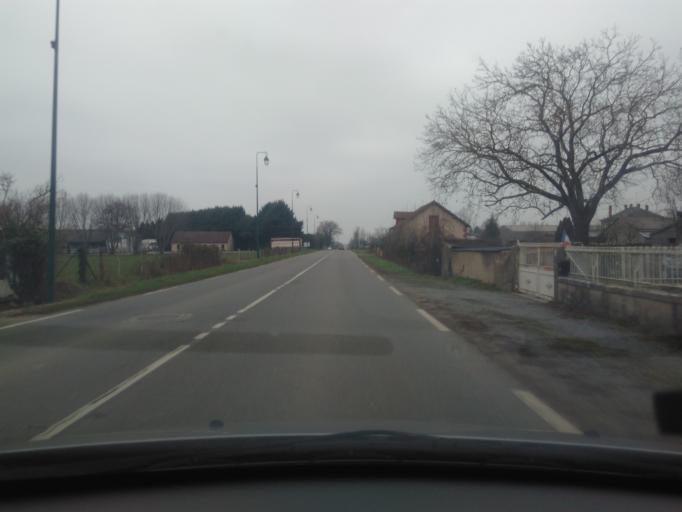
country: FR
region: Centre
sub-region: Departement du Cher
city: Charenton-du-Cher
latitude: 46.7314
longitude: 2.6322
